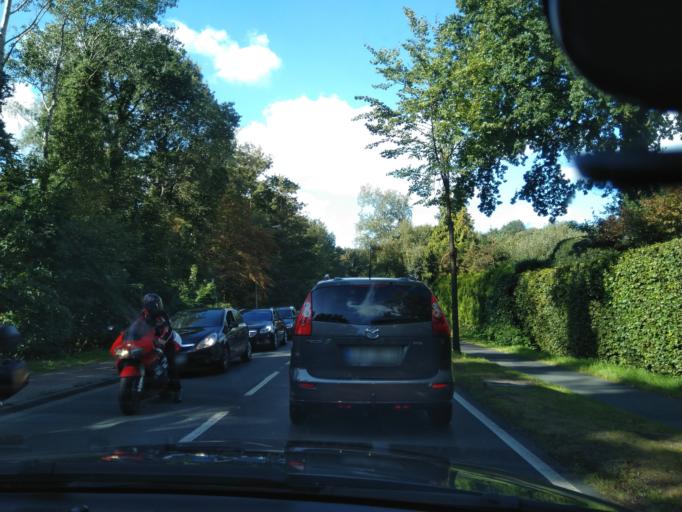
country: DE
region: Lower Saxony
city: Leer
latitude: 53.2512
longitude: 7.4578
